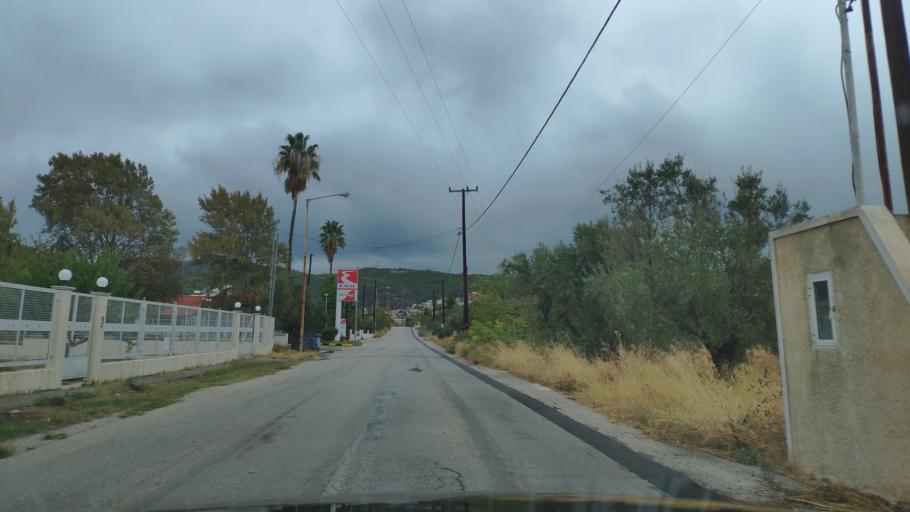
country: GR
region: Peloponnese
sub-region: Nomos Korinthias
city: Perachora
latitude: 38.0182
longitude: 22.9473
